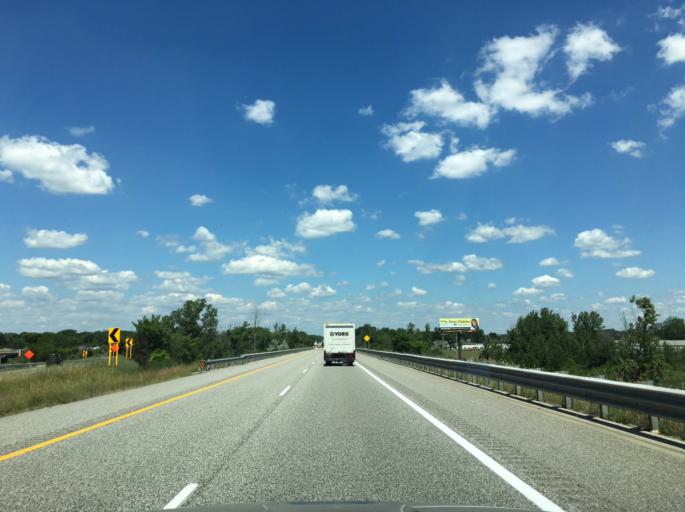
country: US
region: Michigan
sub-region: Midland County
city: Midland
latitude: 43.6098
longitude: -84.1644
